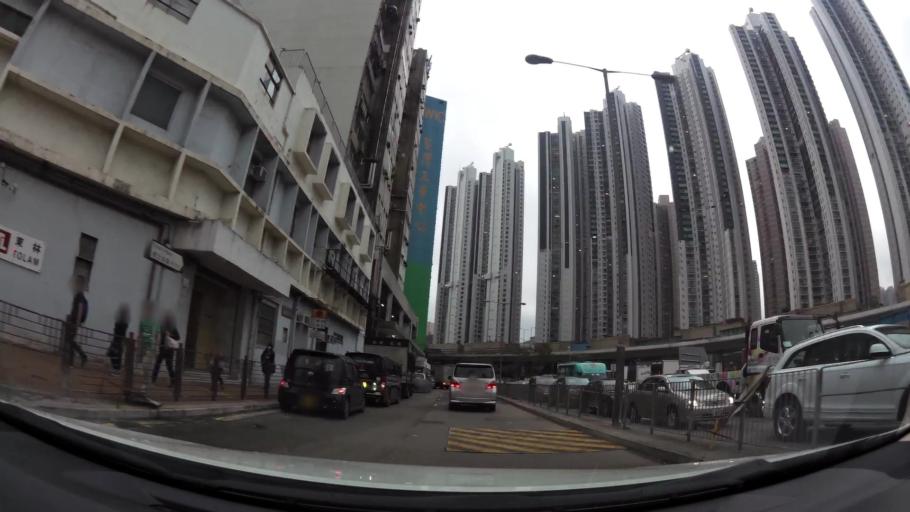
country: HK
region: Tsuen Wan
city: Tsuen Wan
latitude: 22.3664
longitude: 114.1147
